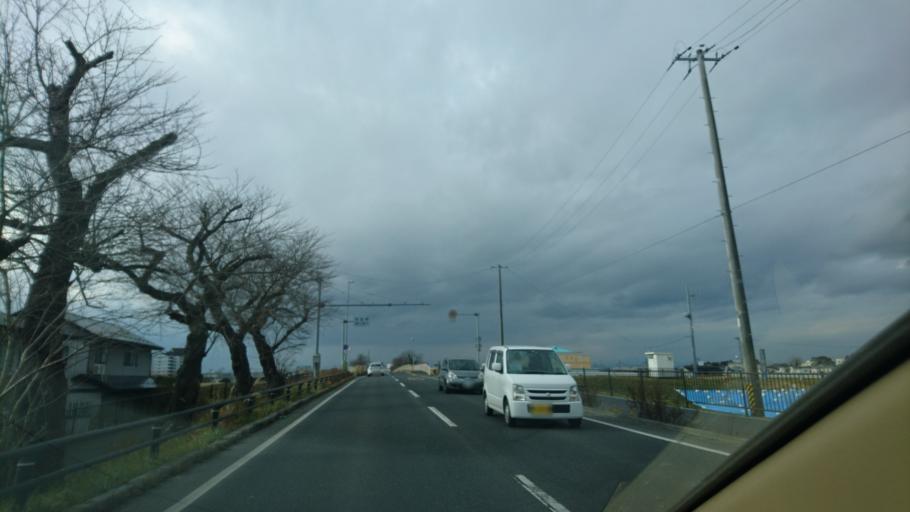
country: JP
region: Miyagi
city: Furukawa
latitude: 38.5702
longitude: 140.9825
